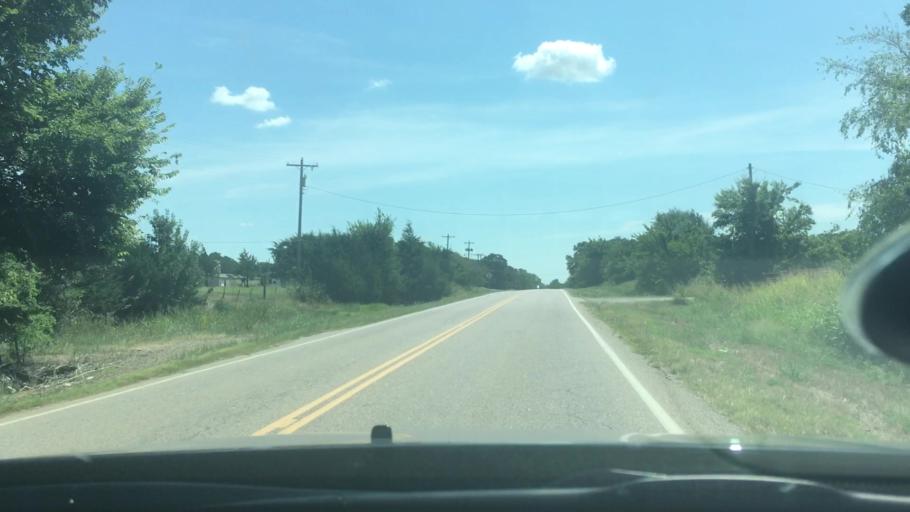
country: US
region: Oklahoma
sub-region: Bryan County
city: Colbert
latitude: 33.8529
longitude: -96.4948
